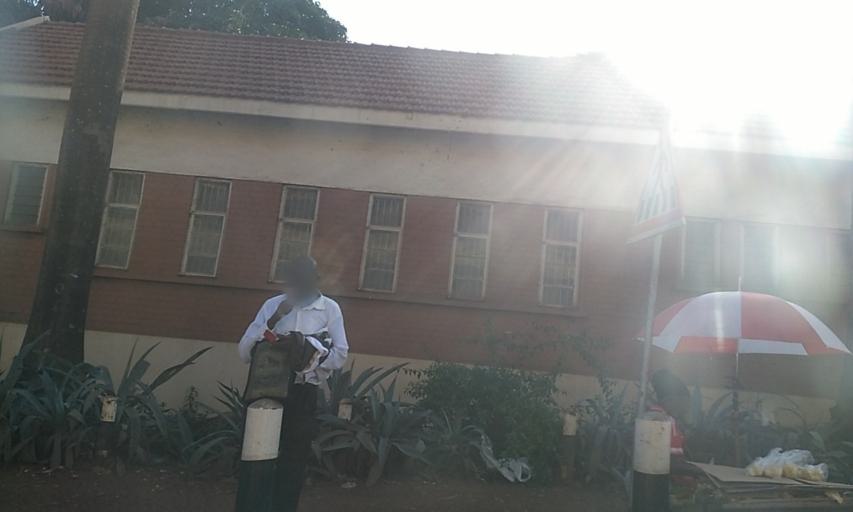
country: UG
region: Central Region
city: Kampala Central Division
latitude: 0.3146
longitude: 32.5712
